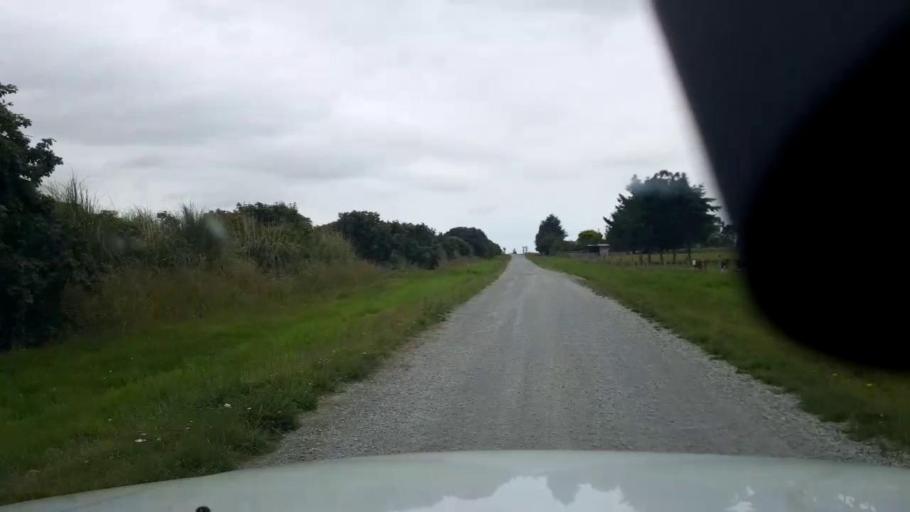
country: NZ
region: Canterbury
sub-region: Timaru District
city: Pleasant Point
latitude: -44.1576
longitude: 171.2841
